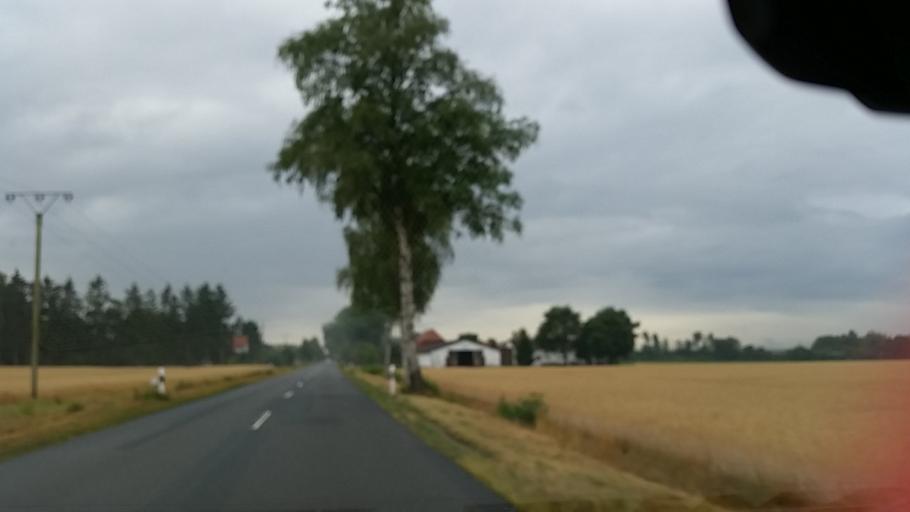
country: DE
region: Lower Saxony
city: Schoneworde
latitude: 52.6026
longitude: 10.6875
